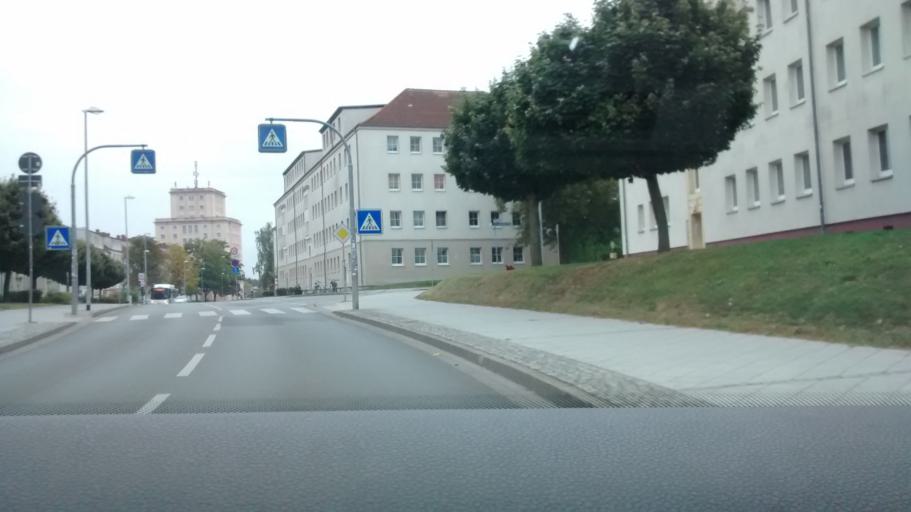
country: DE
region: Mecklenburg-Vorpommern
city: Wismar
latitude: 53.9030
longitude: 11.4205
